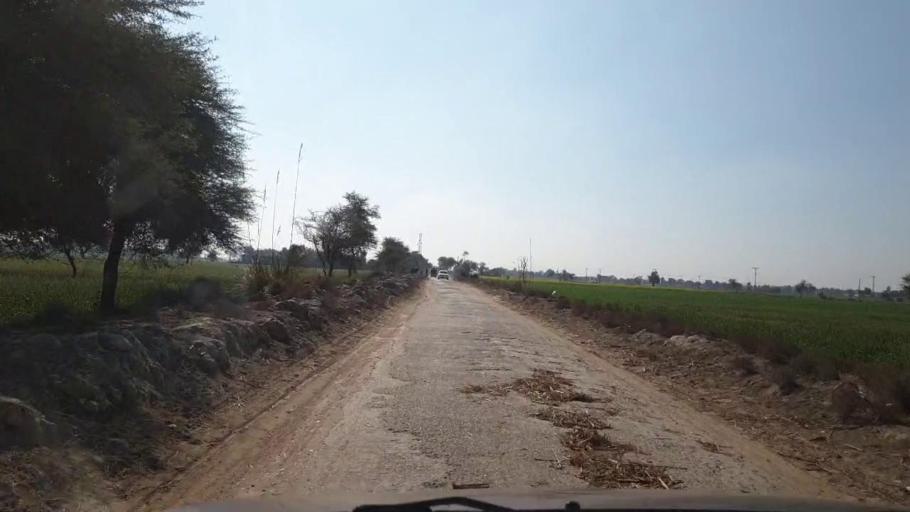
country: PK
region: Sindh
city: Sinjhoro
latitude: 25.9449
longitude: 68.7468
